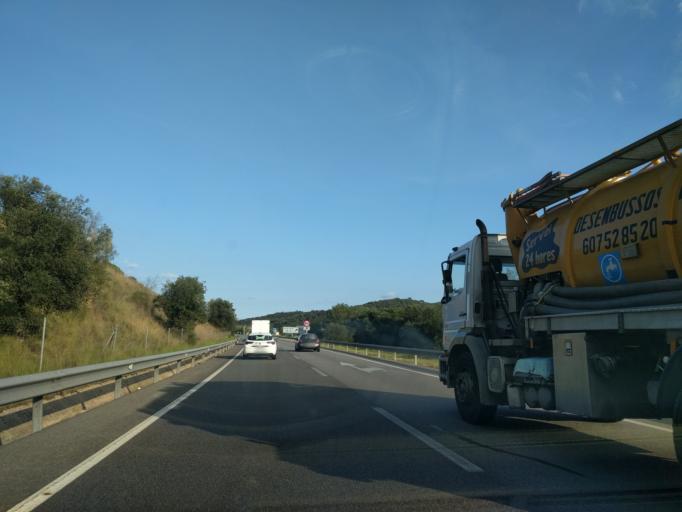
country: ES
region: Catalonia
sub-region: Provincia de Girona
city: Llagostera
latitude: 41.8280
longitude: 2.9410
